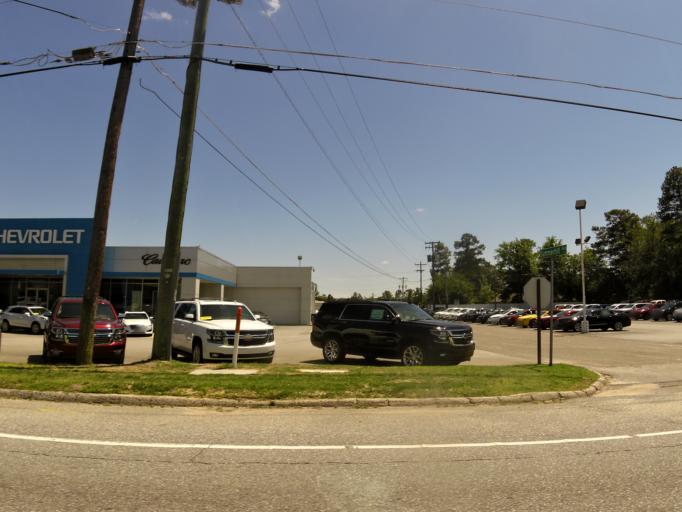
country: US
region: South Carolina
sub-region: Aiken County
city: Warrenville
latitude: 33.5632
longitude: -81.7700
